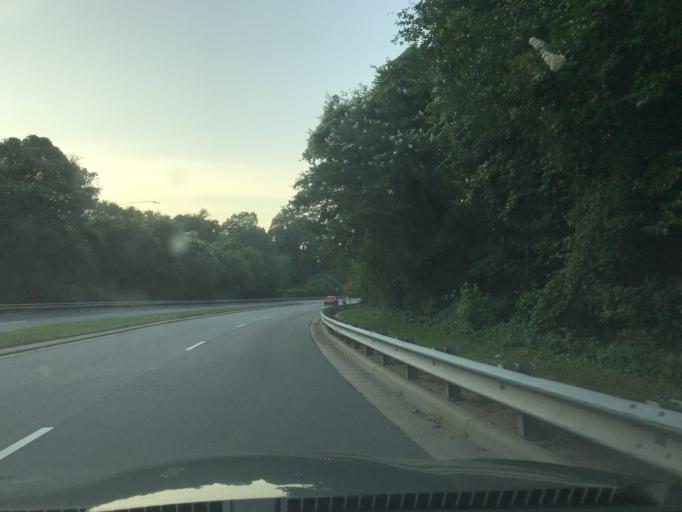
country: US
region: North Carolina
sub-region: Wake County
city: Raleigh
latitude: 35.7758
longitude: -78.6139
